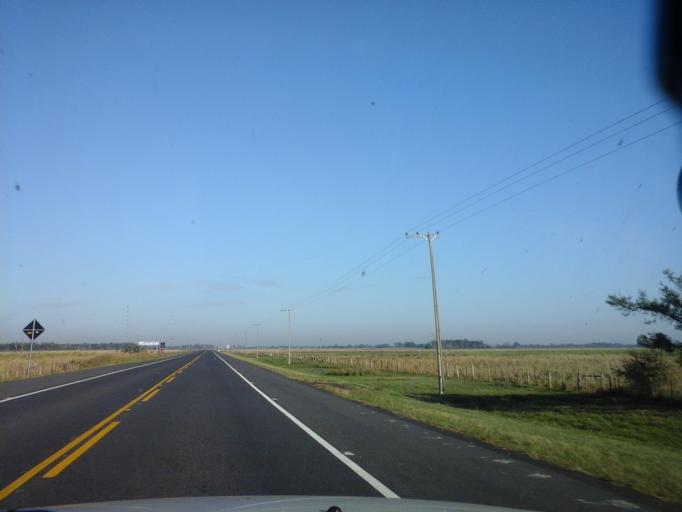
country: PY
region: Neembucu
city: Pilar
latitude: -26.8569
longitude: -57.9845
